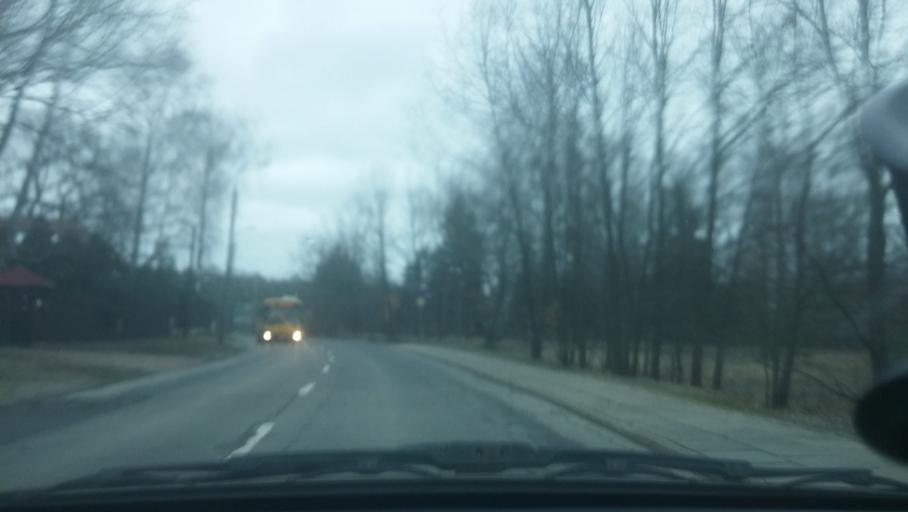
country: PL
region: Masovian Voivodeship
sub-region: Warszawa
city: Bialoleka
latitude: 52.3366
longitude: 21.0013
